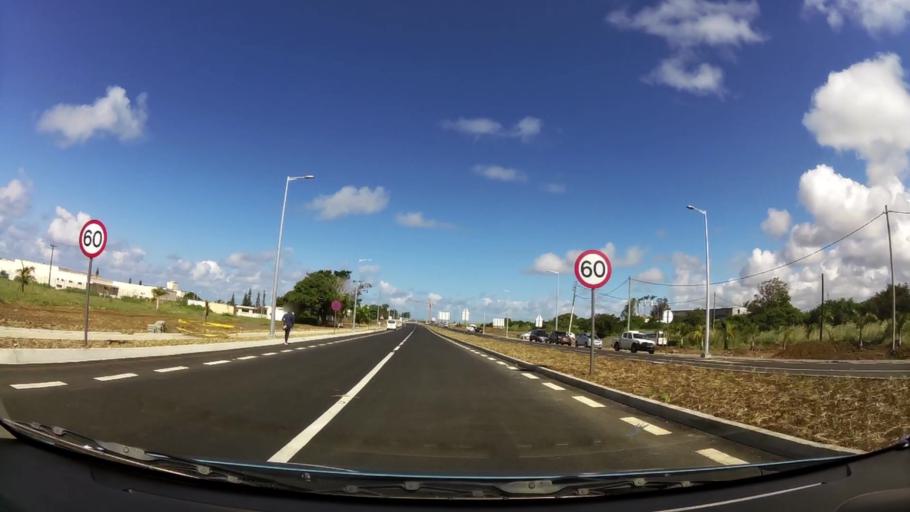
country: MU
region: Grand Port
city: Plaine Magnien
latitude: -20.4352
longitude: 57.6737
